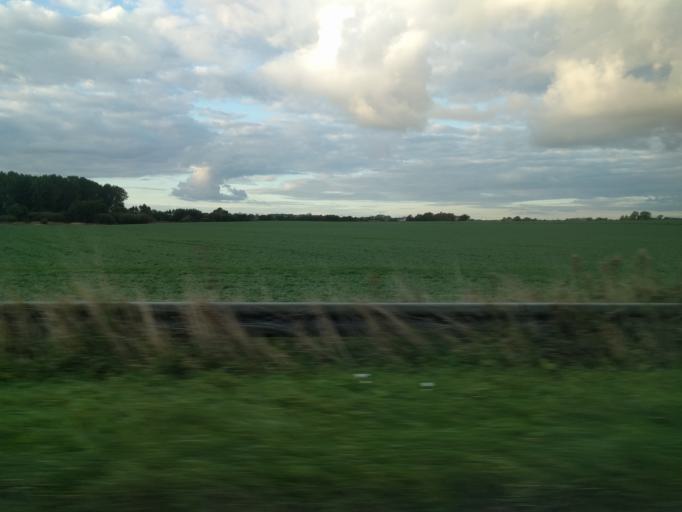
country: DK
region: Zealand
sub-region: Slagelse Kommune
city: Forlev
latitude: 55.3714
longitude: 11.2583
